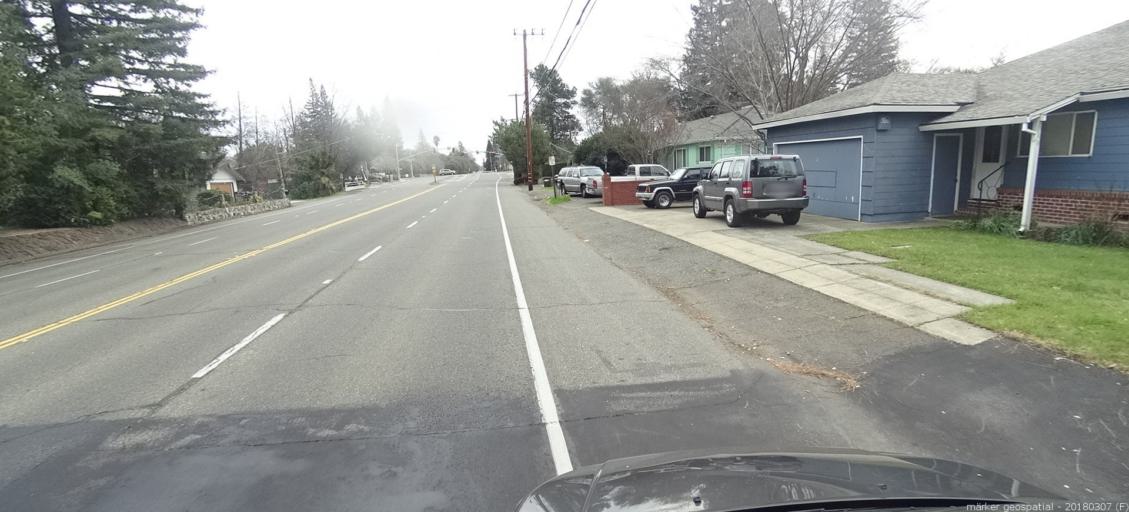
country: US
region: California
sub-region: Sacramento County
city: Carmichael
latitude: 38.6282
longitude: -121.3480
